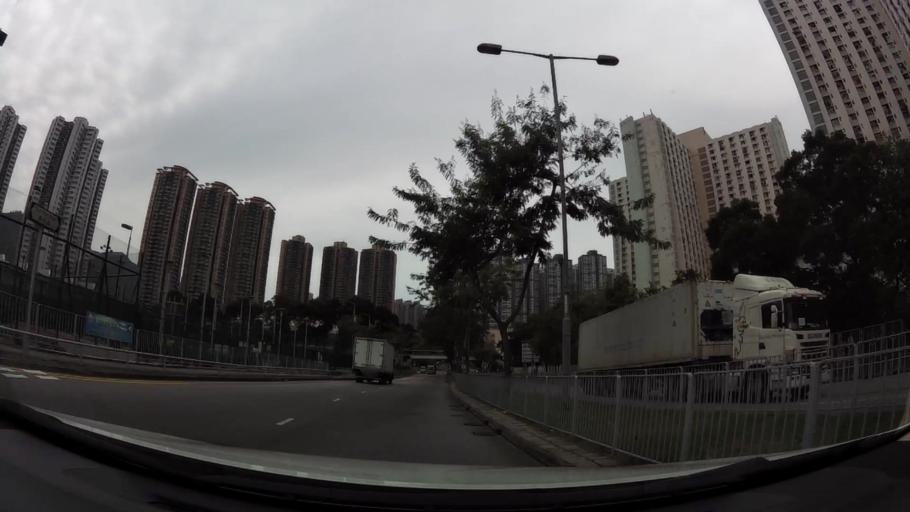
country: HK
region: Tuen Mun
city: Tuen Mun
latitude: 22.4045
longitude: 113.9728
